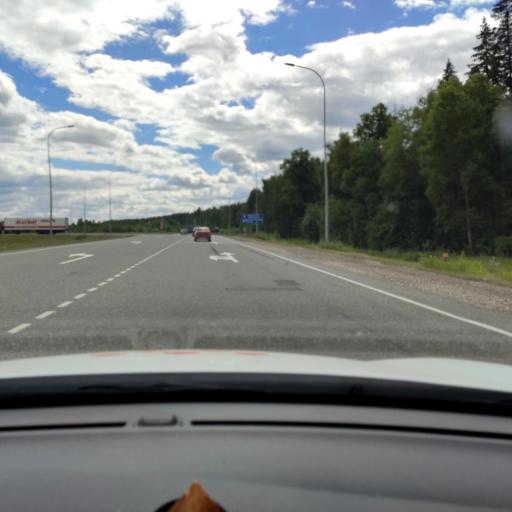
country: RU
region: Tatarstan
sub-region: Zelenodol'skiy Rayon
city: Zelenodolsk
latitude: 55.8908
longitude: 48.5406
